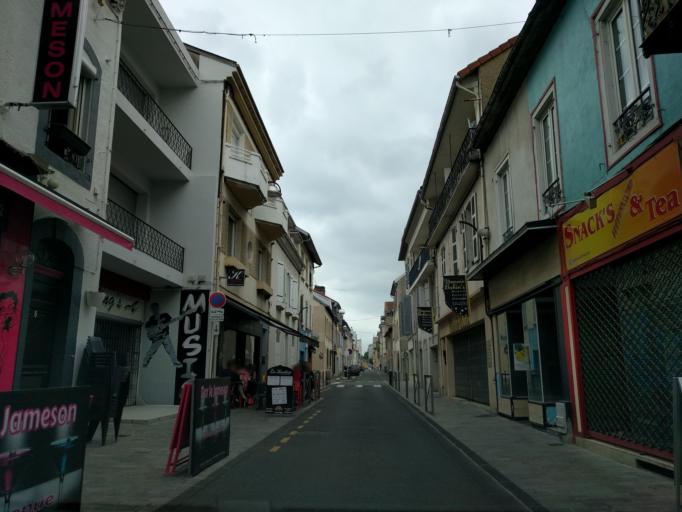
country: FR
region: Midi-Pyrenees
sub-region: Departement des Hautes-Pyrenees
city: Tarbes
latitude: 43.2317
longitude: 0.0779
